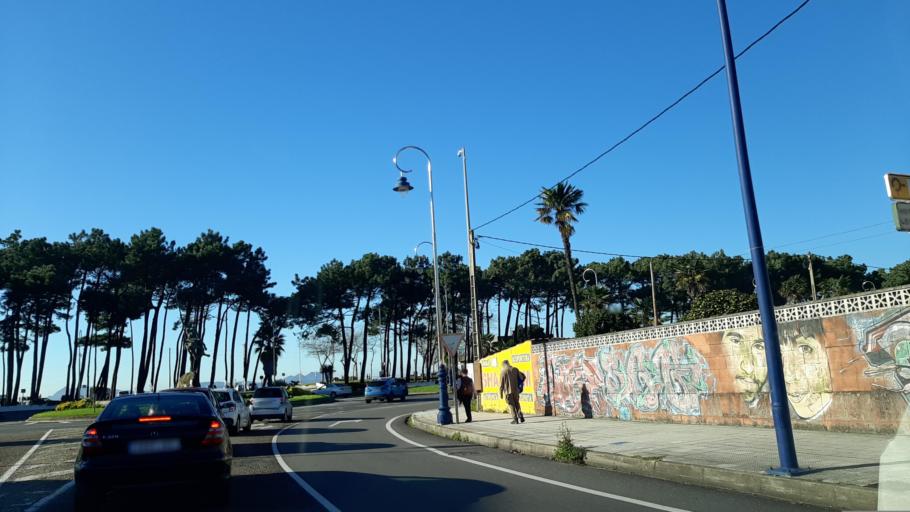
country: ES
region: Galicia
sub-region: Provincia de Pontevedra
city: Cangas
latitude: 42.2112
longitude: -8.7735
